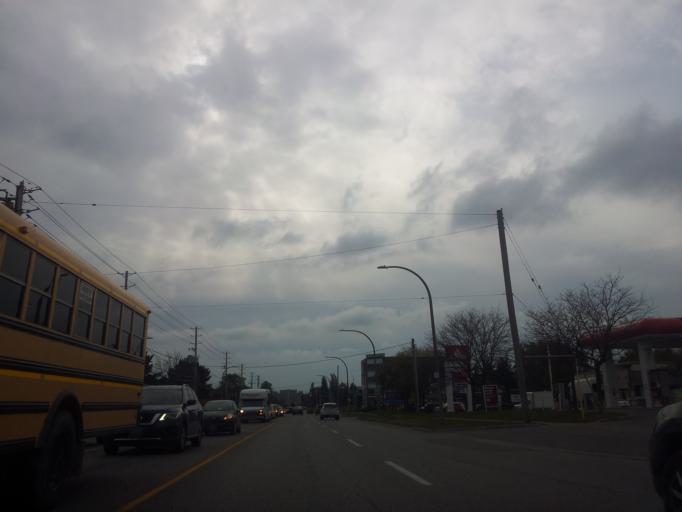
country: CA
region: Ontario
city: London
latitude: 43.0266
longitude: -81.2826
